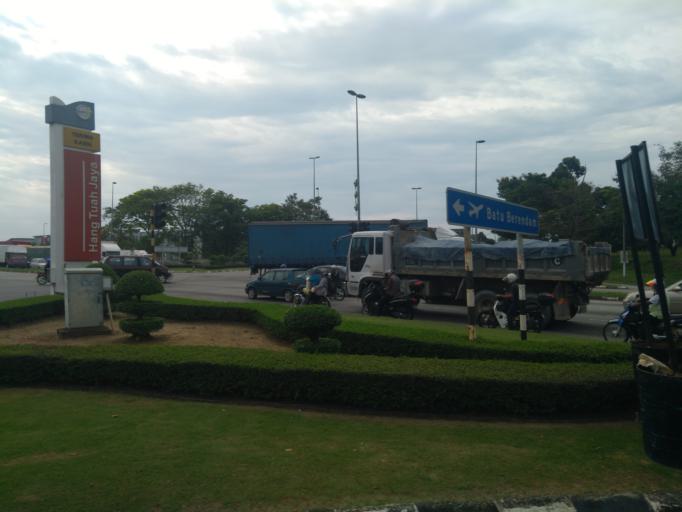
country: MY
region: Melaka
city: Kampung Ayer Keroh
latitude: 2.2867
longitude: 102.2624
